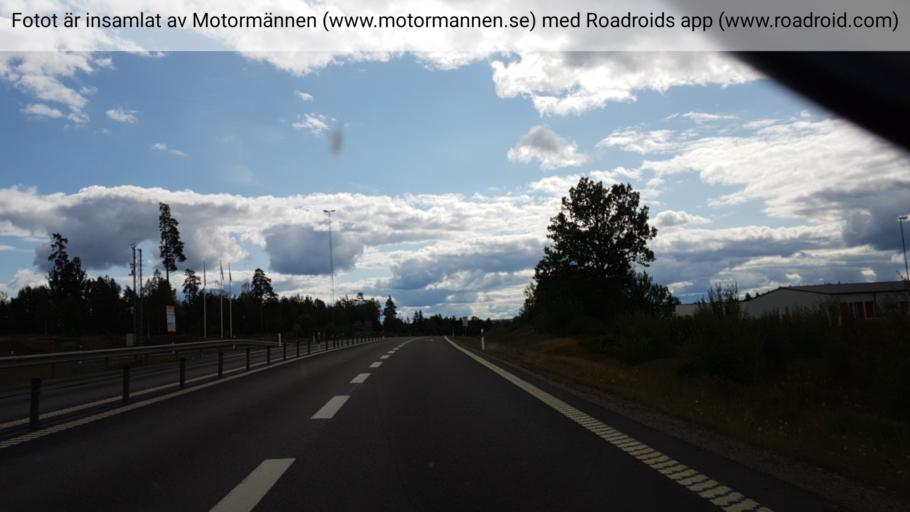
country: SE
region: Joenkoeping
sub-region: Tranas Kommun
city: Tranas
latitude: 58.0333
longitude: 14.9509
